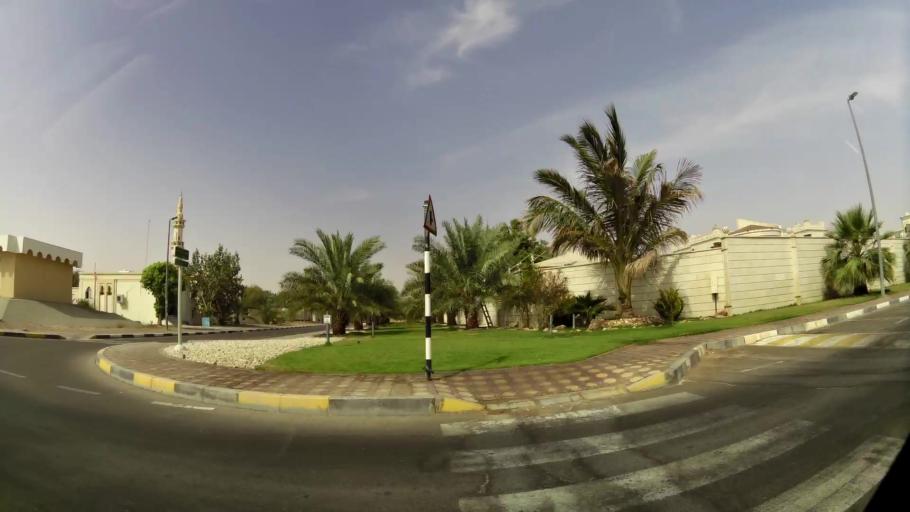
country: AE
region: Abu Dhabi
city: Al Ain
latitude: 24.1670
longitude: 55.7072
